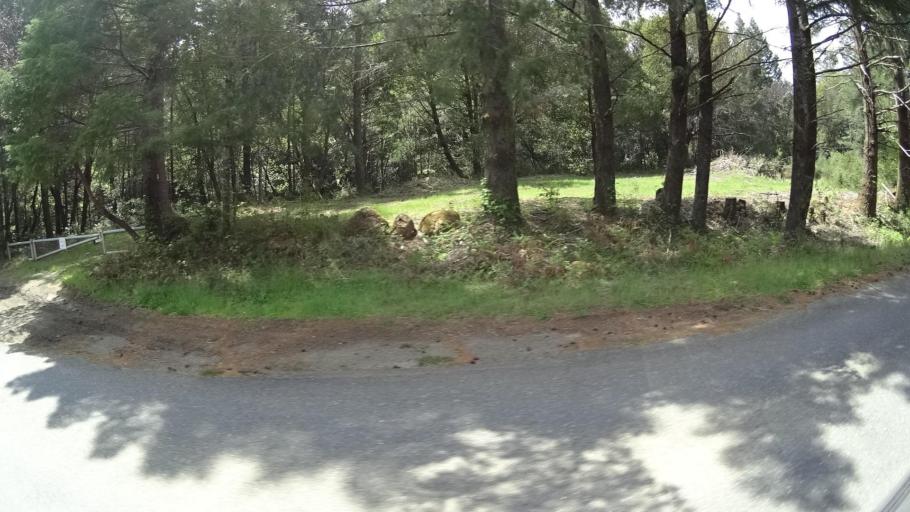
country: US
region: California
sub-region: Humboldt County
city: Redway
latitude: 40.0622
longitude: -123.9625
